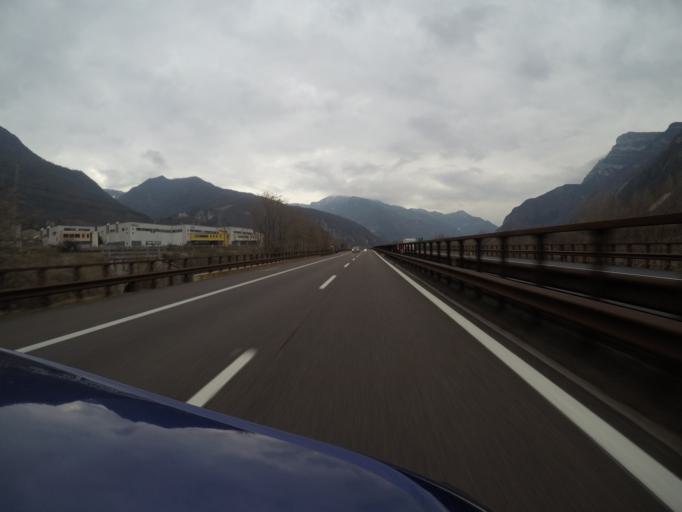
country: IT
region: Trentino-Alto Adige
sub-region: Provincia di Trento
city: Ala
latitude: 45.7937
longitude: 11.0210
